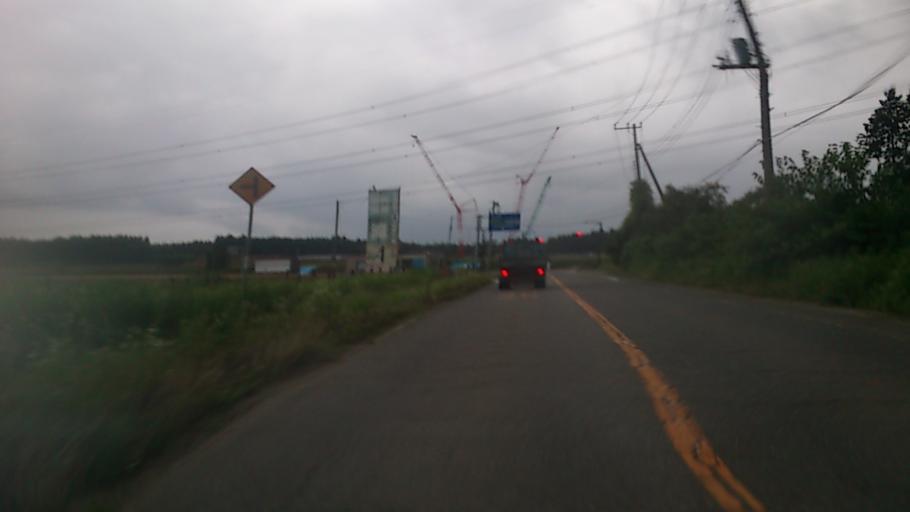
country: JP
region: Ibaraki
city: Ami
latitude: 35.9827
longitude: 140.2266
